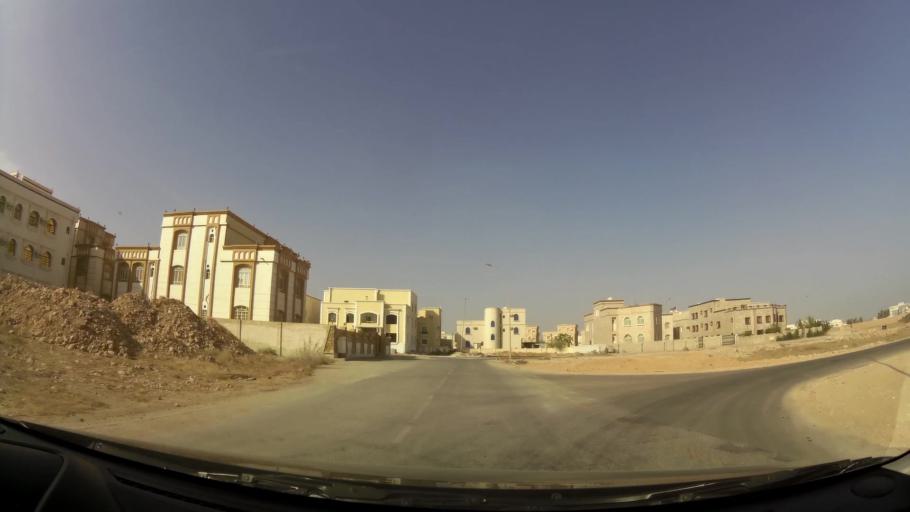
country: OM
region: Zufar
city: Salalah
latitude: 17.0081
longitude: 54.0240
